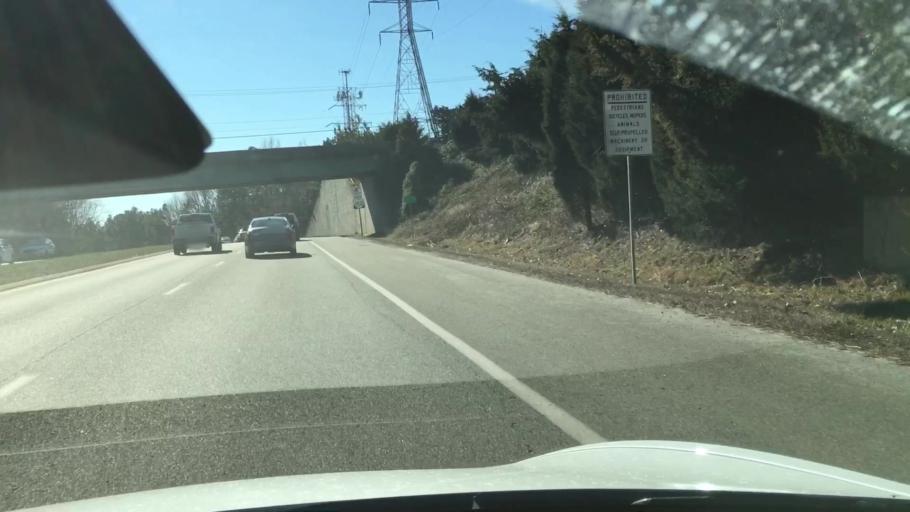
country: US
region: Virginia
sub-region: Henrico County
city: Tuckahoe
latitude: 37.5722
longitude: -77.5763
